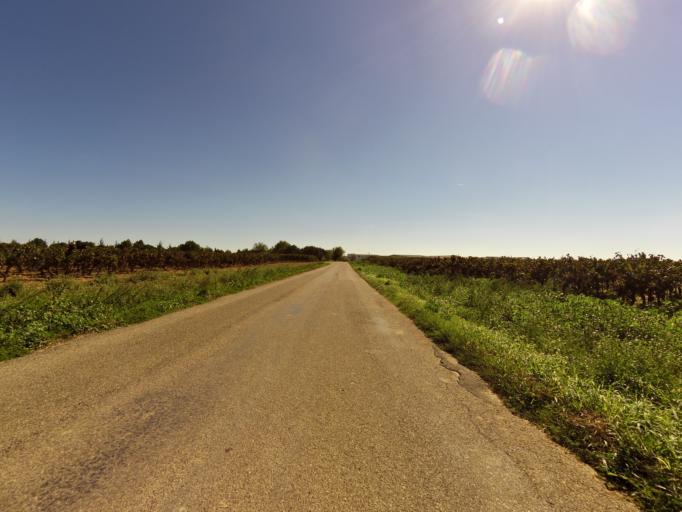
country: FR
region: Languedoc-Roussillon
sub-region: Departement du Gard
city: Codognan
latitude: 43.7288
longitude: 4.2101
